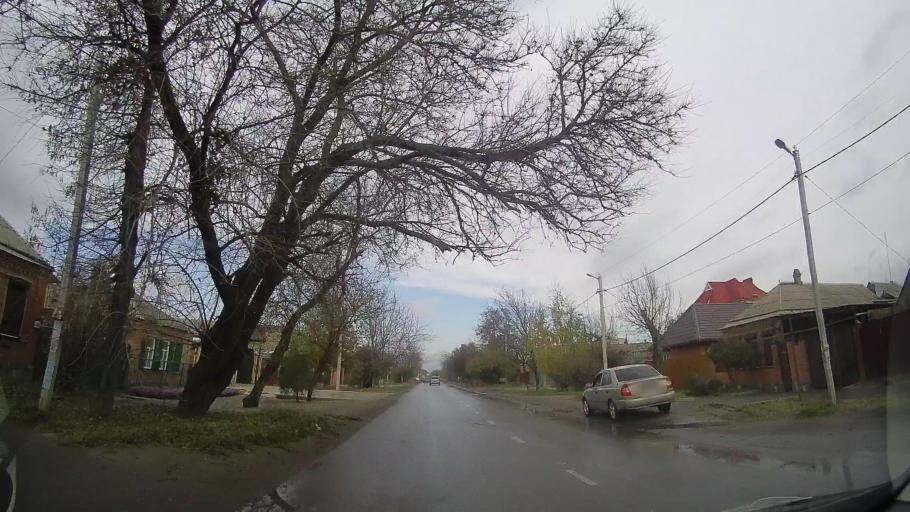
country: RU
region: Rostov
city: Bataysk
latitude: 47.1307
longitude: 39.7679
